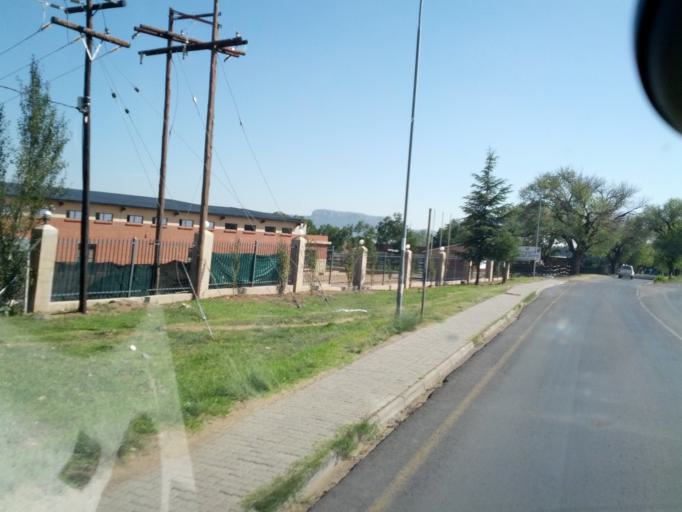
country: LS
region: Maseru
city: Maseru
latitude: -29.3016
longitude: 27.5018
